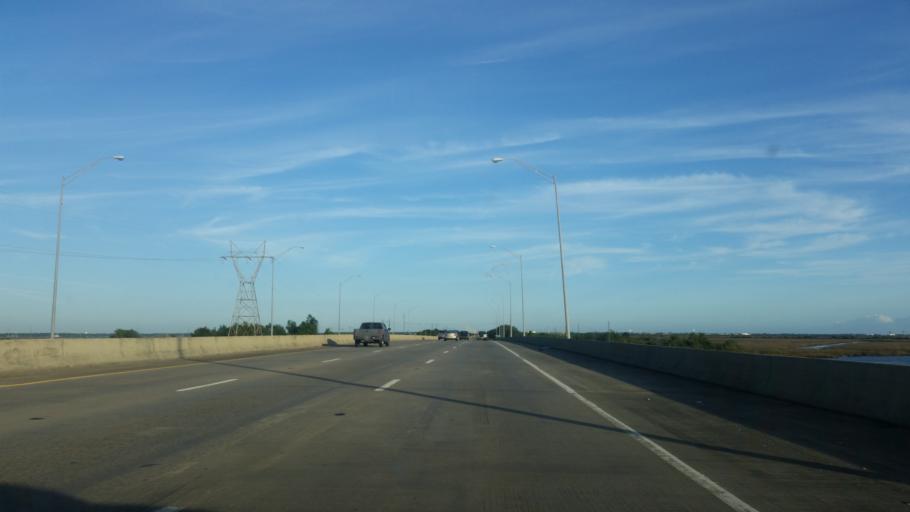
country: US
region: Mississippi
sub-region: Jackson County
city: Gautier
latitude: 30.3828
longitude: -88.6084
